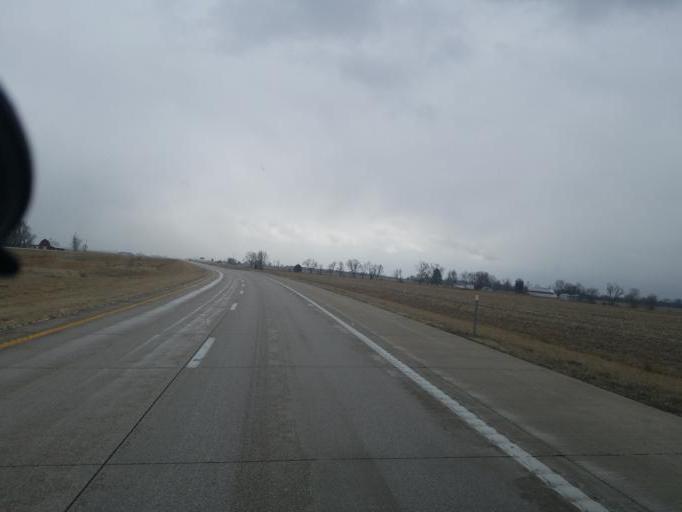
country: US
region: Missouri
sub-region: Randolph County
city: Huntsville
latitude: 39.5732
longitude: -92.4656
